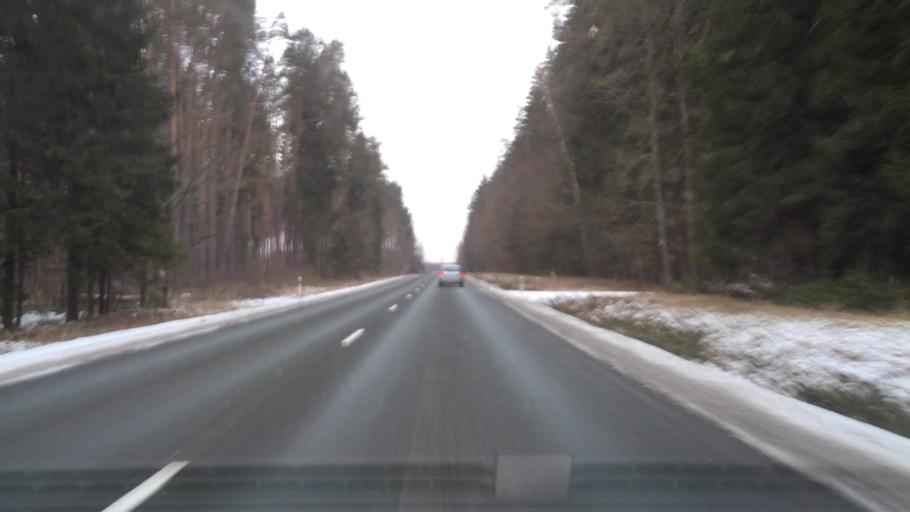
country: LV
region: Valmieras Rajons
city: Valmiera
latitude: 57.5039
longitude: 25.4201
